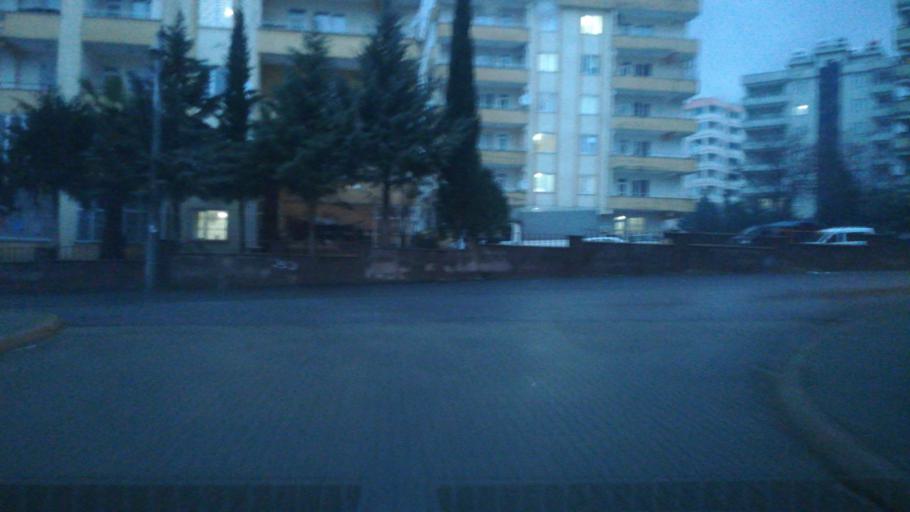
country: TR
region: Kahramanmaras
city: Kahramanmaras
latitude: 37.5951
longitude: 36.9000
